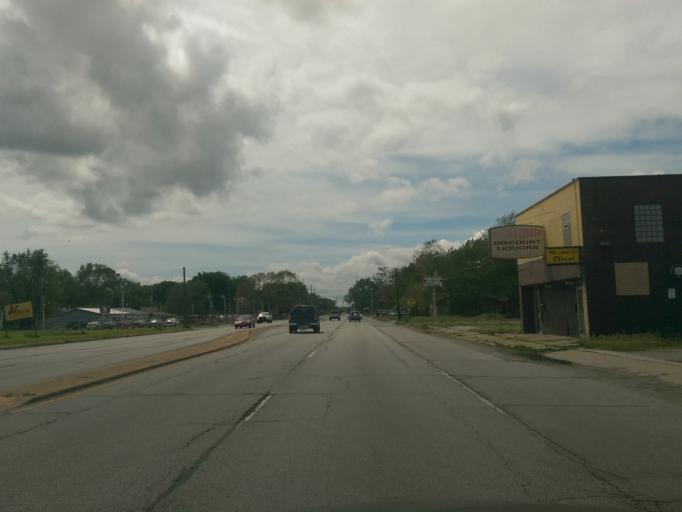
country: US
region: Indiana
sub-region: Lake County
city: East Chicago
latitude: 41.6020
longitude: -87.4095
